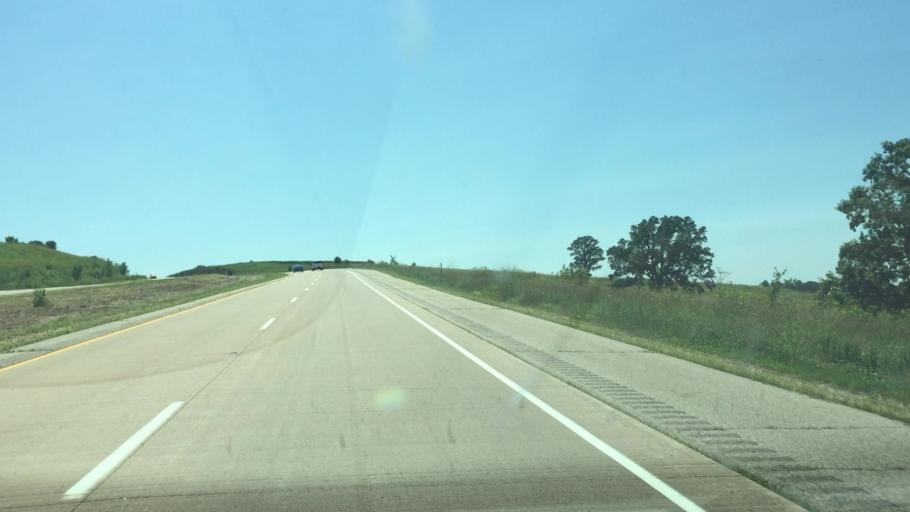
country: US
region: Wisconsin
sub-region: Iowa County
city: Mineral Point
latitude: 42.8085
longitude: -90.2661
